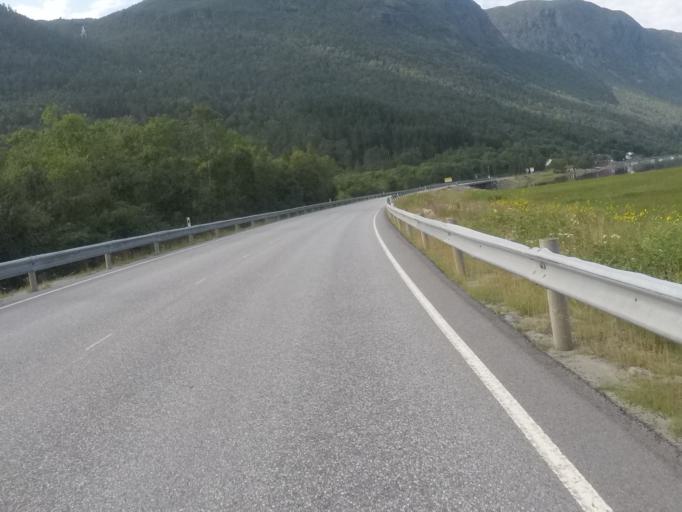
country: NO
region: More og Romsdal
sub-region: Rauma
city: Andalsnes
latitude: 62.5730
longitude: 7.7879
